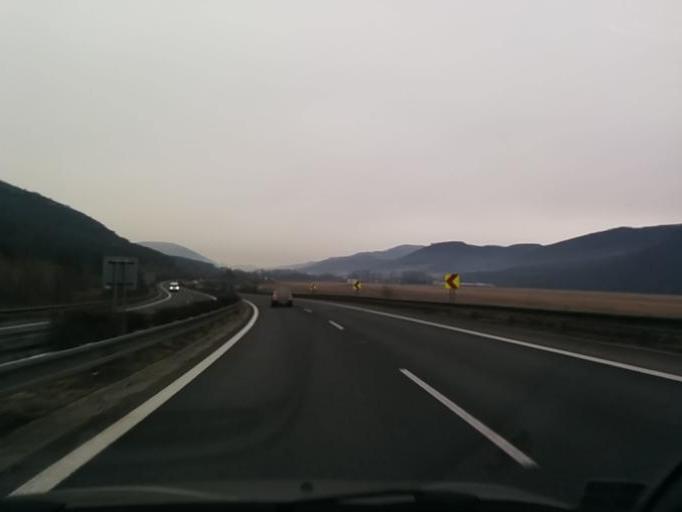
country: SK
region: Banskobystricky
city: Nova Bana
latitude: 48.3633
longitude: 18.5820
